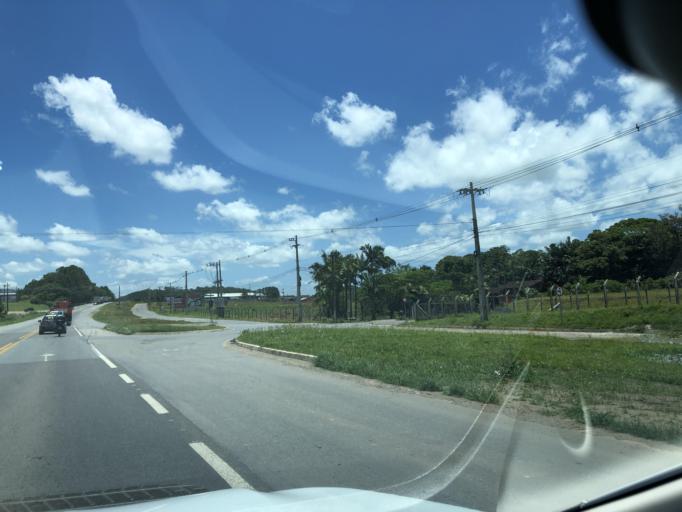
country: BR
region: Santa Catarina
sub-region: Joinville
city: Joinville
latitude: -26.4250
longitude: -48.7861
